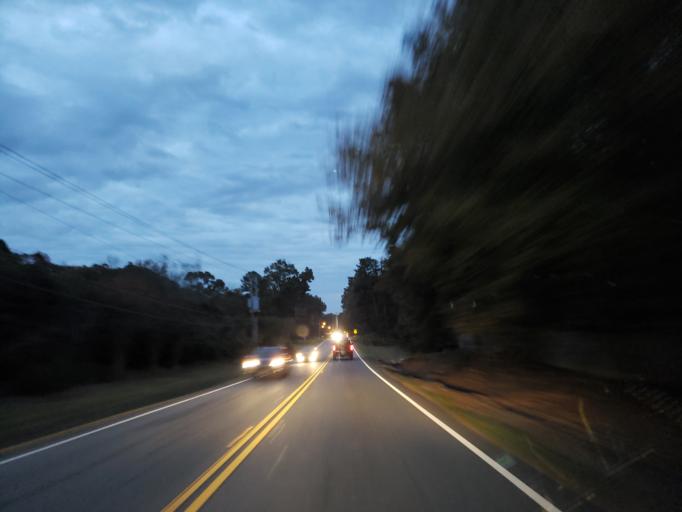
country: US
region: Georgia
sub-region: Cobb County
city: Powder Springs
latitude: 33.9226
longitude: -84.6944
